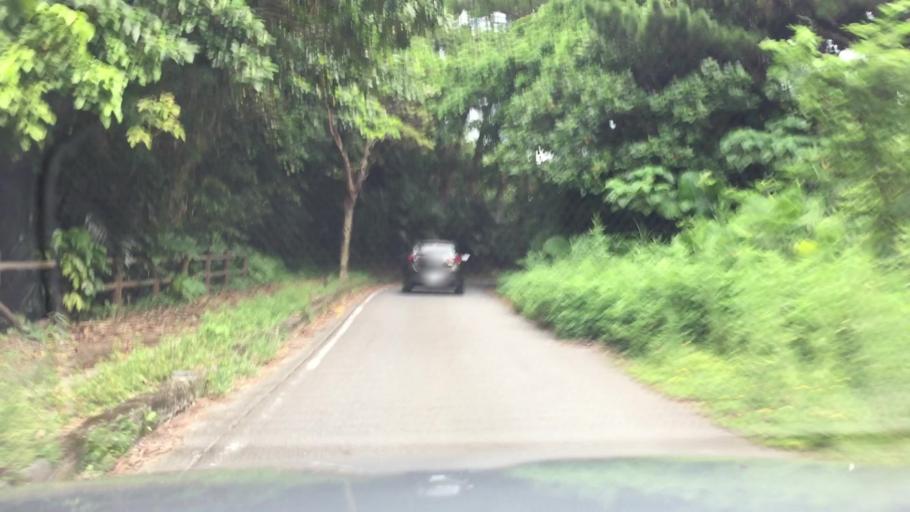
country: JP
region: Okinawa
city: Ishigaki
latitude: 24.4531
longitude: 124.1373
